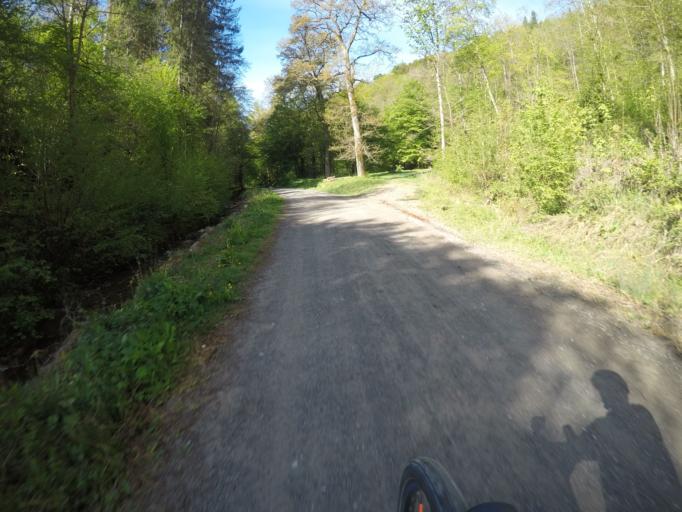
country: DE
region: Baden-Wuerttemberg
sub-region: Tuebingen Region
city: Tuebingen
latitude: 48.5529
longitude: 9.0786
